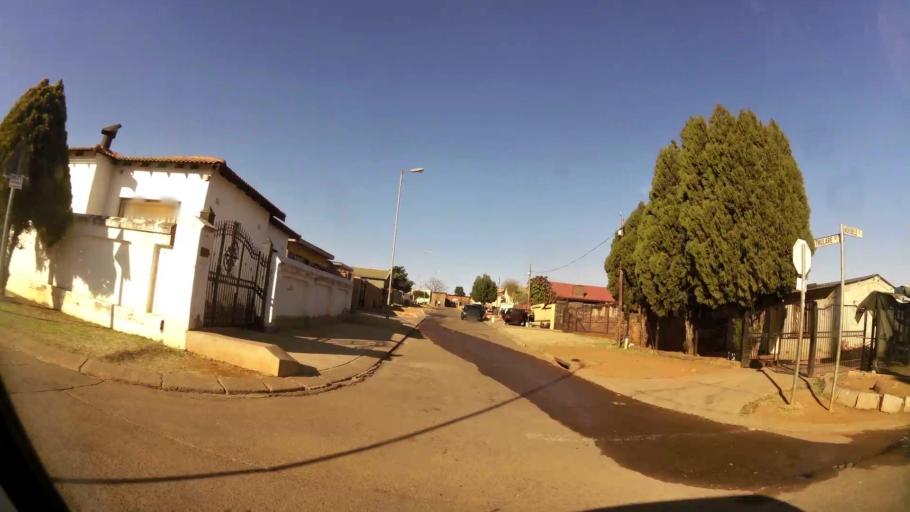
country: ZA
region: Gauteng
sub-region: City of Tshwane Metropolitan Municipality
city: Cullinan
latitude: -25.7040
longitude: 28.3692
